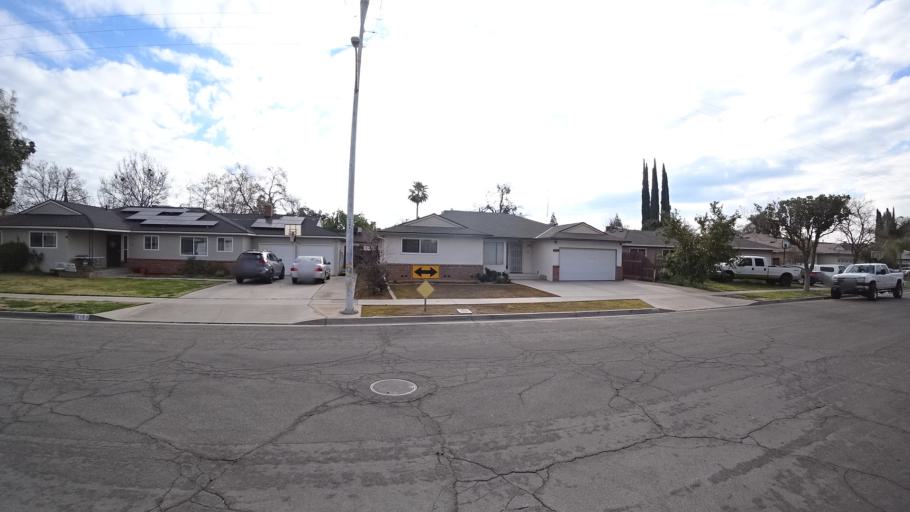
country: US
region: California
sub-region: Fresno County
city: Clovis
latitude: 36.8260
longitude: -119.7642
